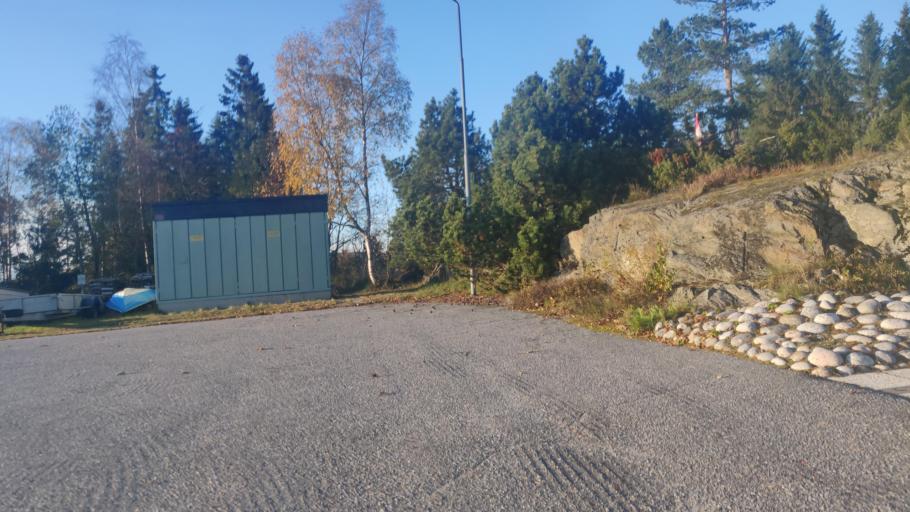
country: SE
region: Vaesternorrland
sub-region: Sundsvalls Kommun
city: Njurundabommen
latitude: 62.2746
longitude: 17.3998
